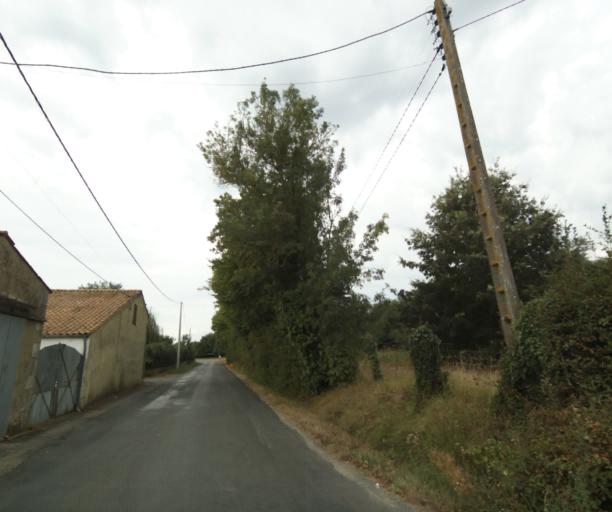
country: FR
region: Poitou-Charentes
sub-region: Departement de la Charente-Maritime
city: Tonnay-Charente
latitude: 45.9567
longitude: -0.8782
